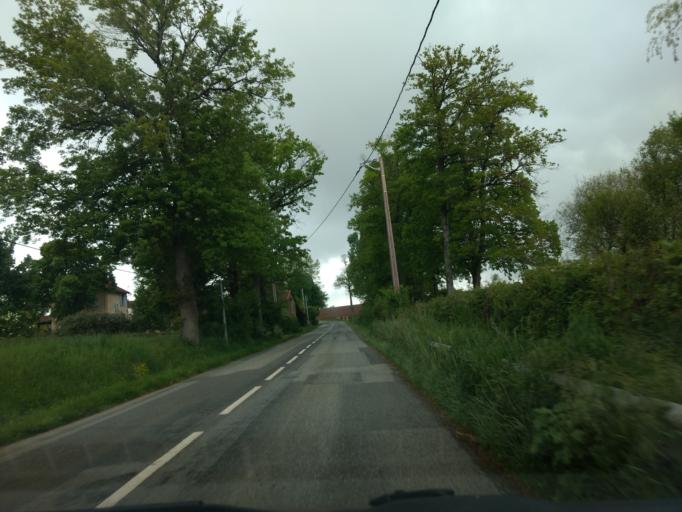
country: FR
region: Midi-Pyrenees
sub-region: Departement de l'Aveyron
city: Montbazens
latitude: 44.4909
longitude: 2.2172
